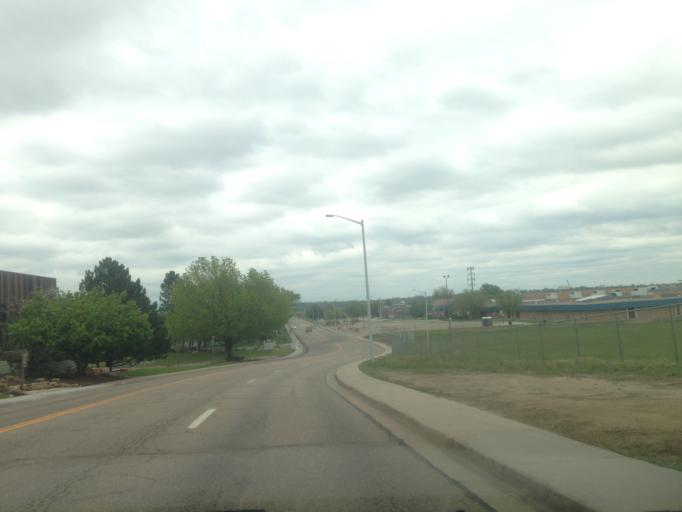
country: US
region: Colorado
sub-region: Boulder County
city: Longmont
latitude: 40.1420
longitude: -105.1216
